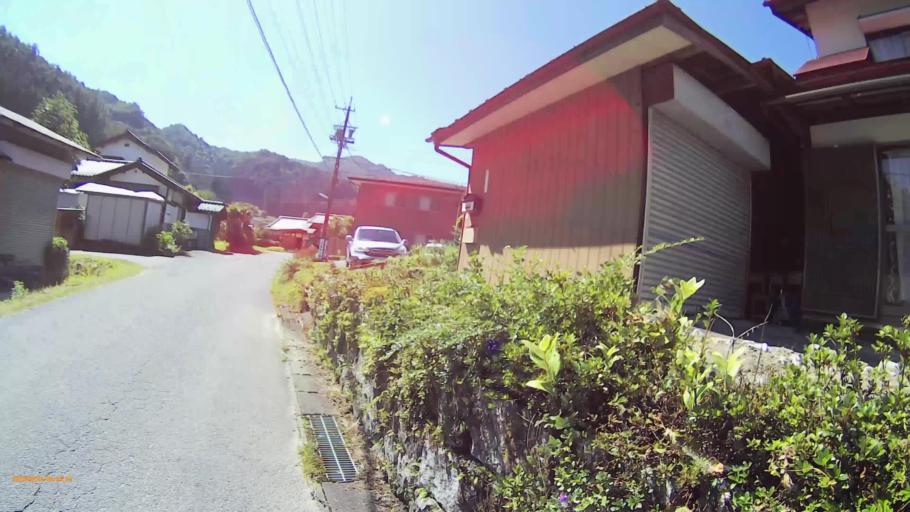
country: JP
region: Nagano
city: Iida
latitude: 35.6865
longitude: 137.6745
